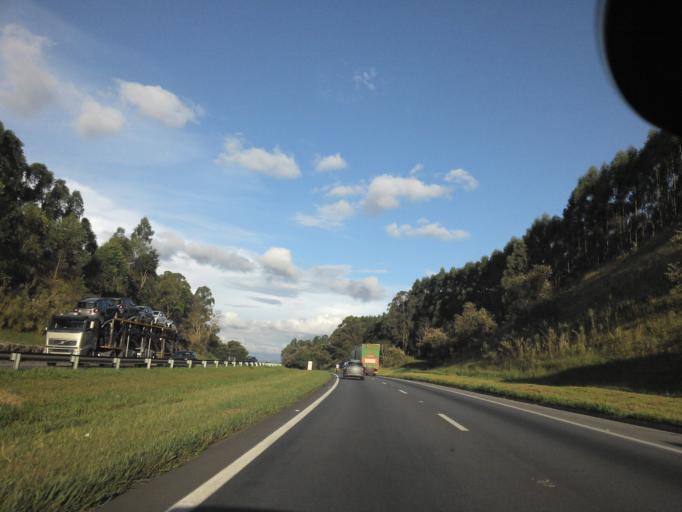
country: BR
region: Sao Paulo
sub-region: Jarinu
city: Jarinu
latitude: -23.0355
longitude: -46.7268
